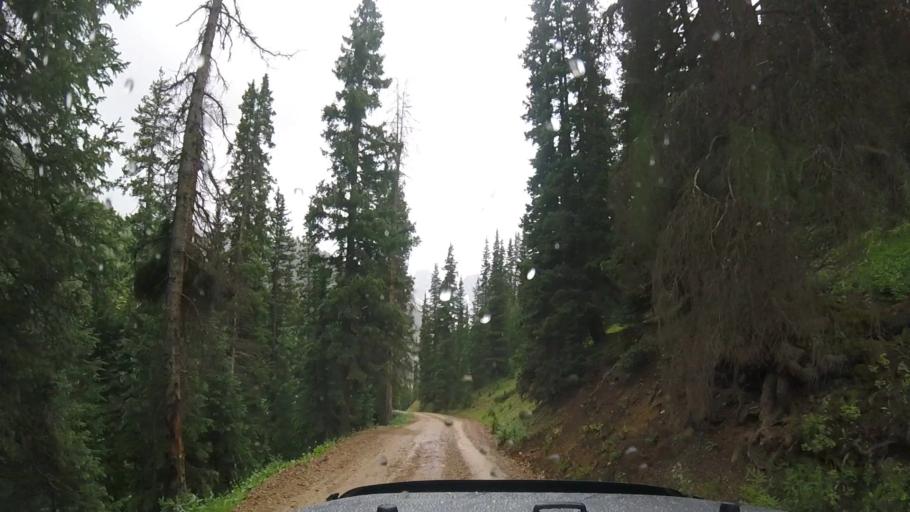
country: US
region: Colorado
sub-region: San Juan County
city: Silverton
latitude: 37.9009
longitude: -107.6472
